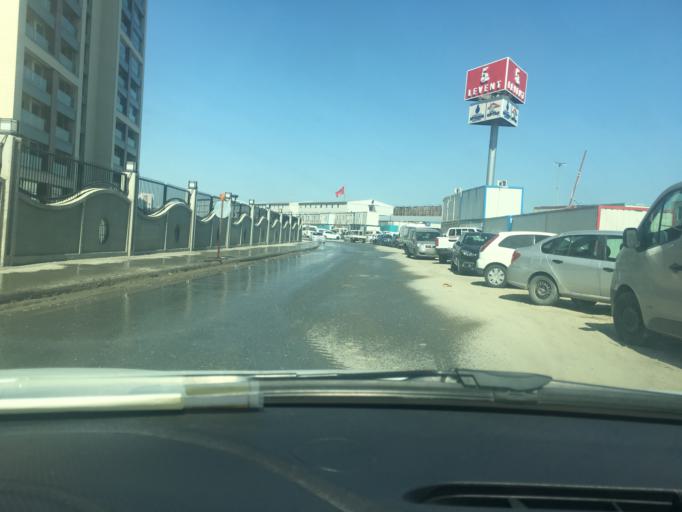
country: TR
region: Istanbul
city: Sisli
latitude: 41.0922
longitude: 28.9499
